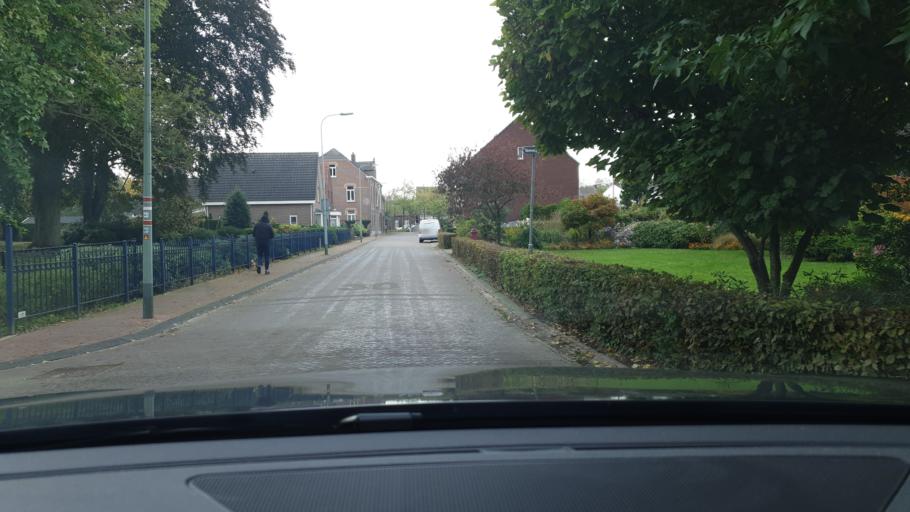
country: NL
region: Limburg
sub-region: Gemeente Venlo
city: Arcen
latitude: 51.4605
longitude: 6.1647
